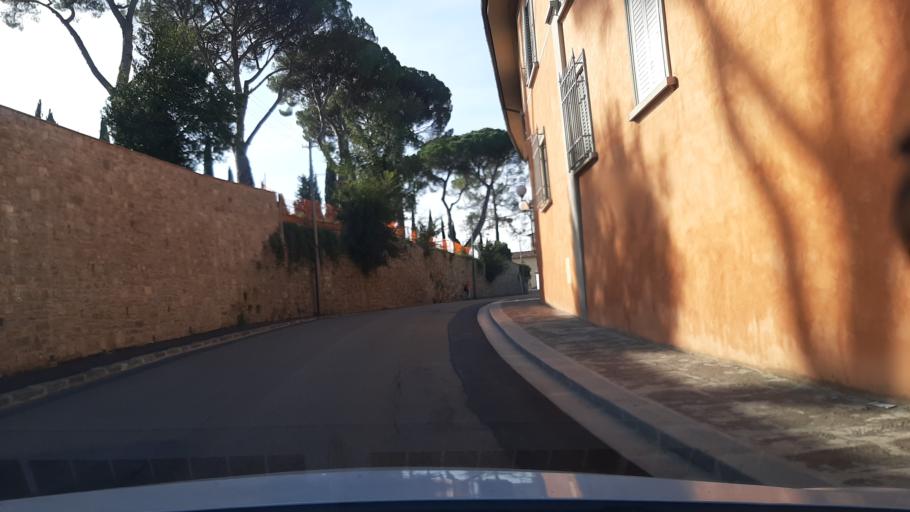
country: IT
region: Tuscany
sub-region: Province of Florence
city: Florence
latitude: 43.7526
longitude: 11.2569
